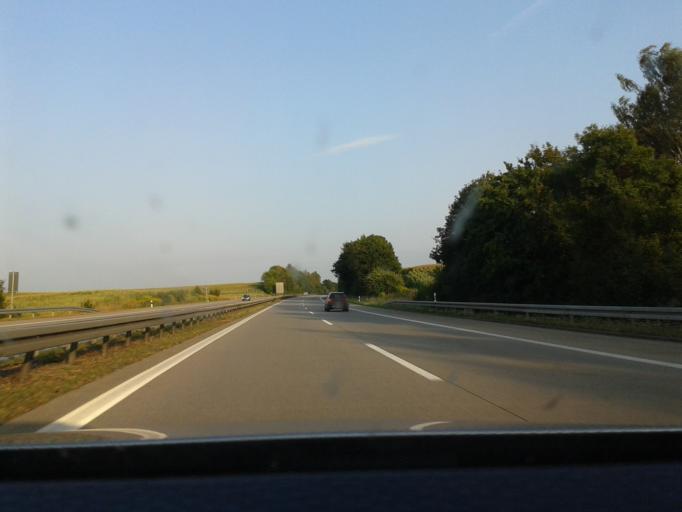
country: DE
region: Saxony
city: Dobeln
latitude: 51.1529
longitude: 13.1338
